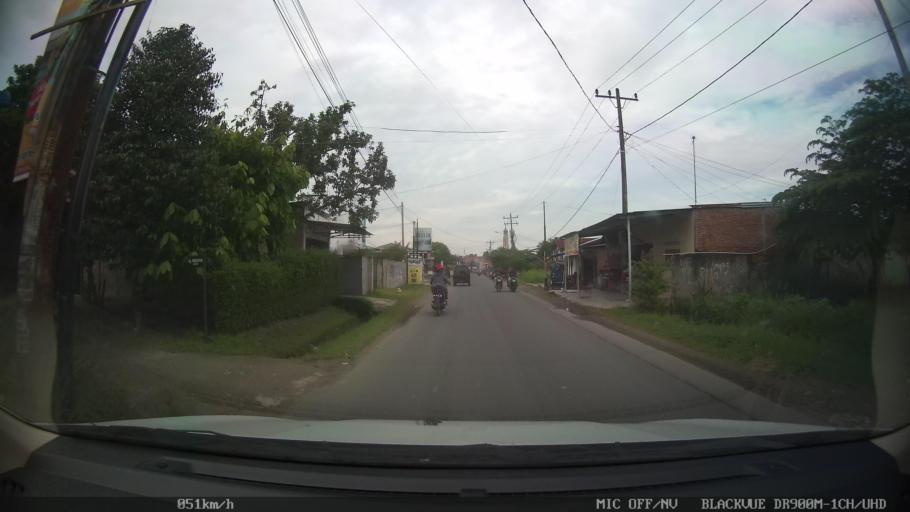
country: ID
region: North Sumatra
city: Sunggal
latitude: 3.6204
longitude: 98.5992
